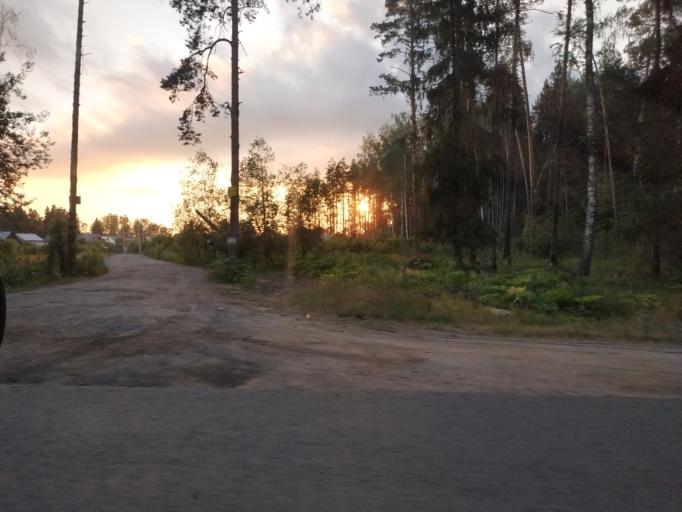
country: RU
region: Moskovskaya
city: Krasnoarmeysk
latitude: 56.0318
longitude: 38.1868
